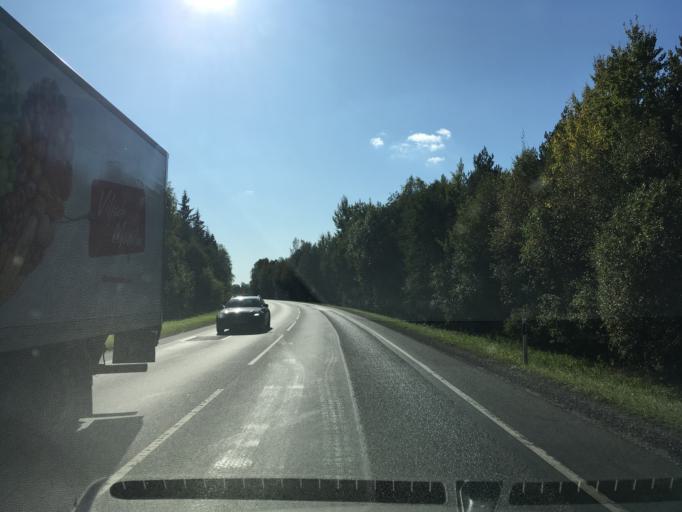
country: EE
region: Harju
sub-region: Nissi vald
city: Turba
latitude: 59.0670
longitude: 24.1949
